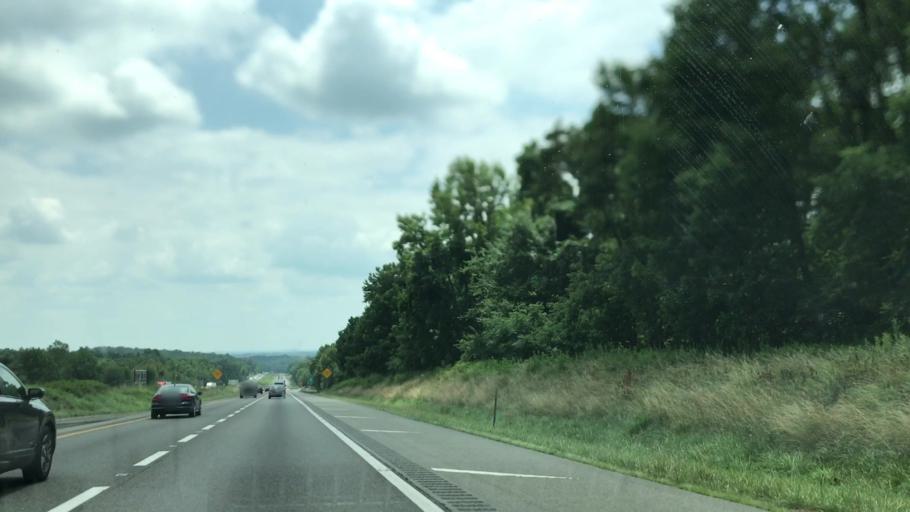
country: US
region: Virginia
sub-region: Carroll County
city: Cana
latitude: 36.5822
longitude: -80.7426
